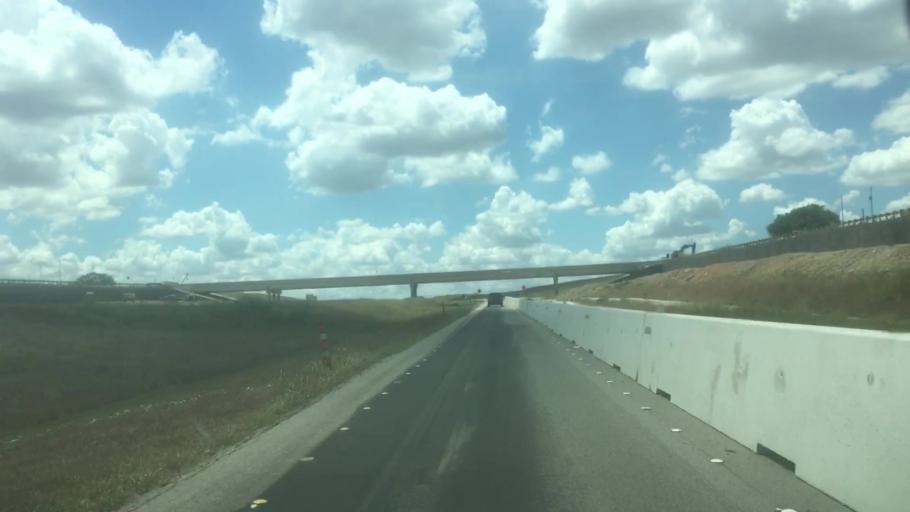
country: US
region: Texas
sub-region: Caldwell County
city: Lockhart
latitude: 29.8538
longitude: -97.7187
